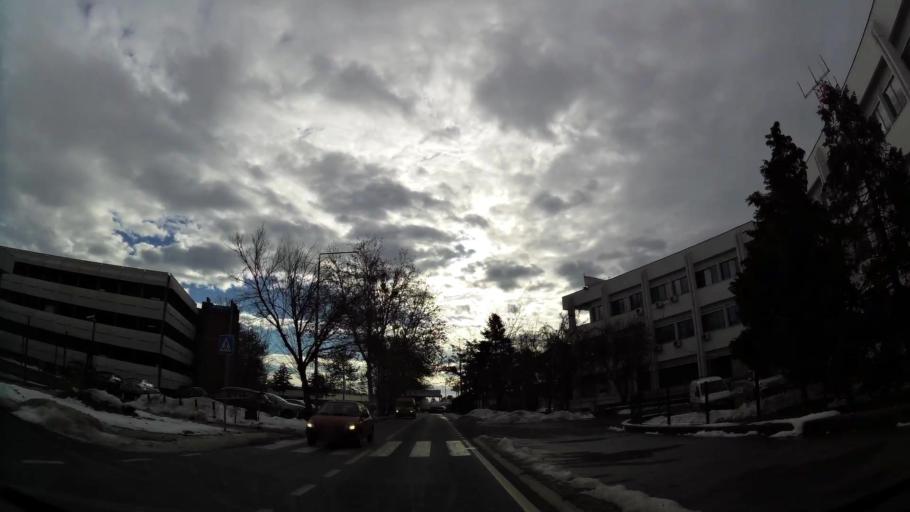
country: RS
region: Central Serbia
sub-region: Belgrade
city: Surcin
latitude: 44.8185
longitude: 20.2878
